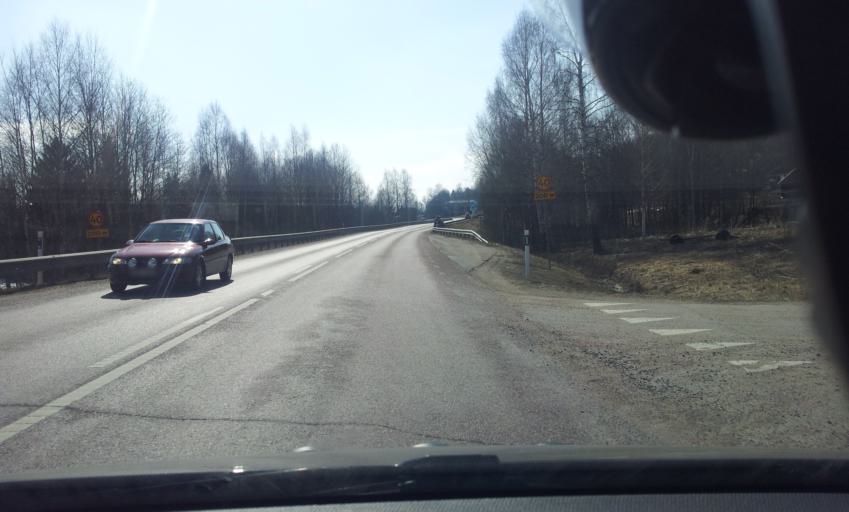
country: SE
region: Gaevleborg
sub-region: Ljusdals Kommun
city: Jaervsoe
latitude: 61.7252
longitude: 16.1686
